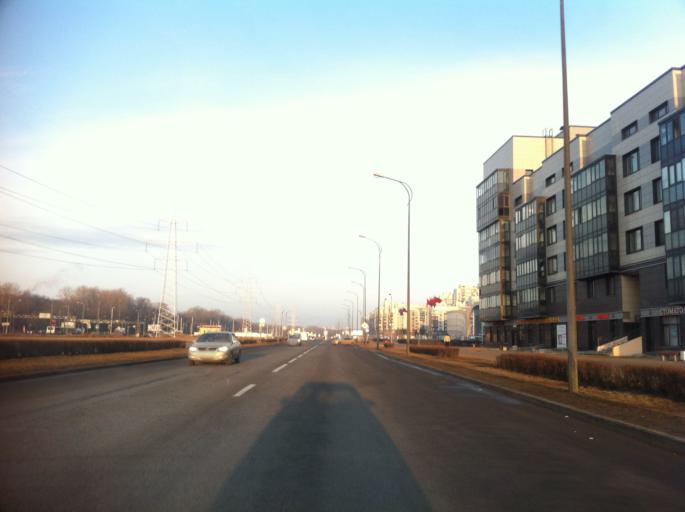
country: RU
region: St.-Petersburg
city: Sosnovaya Polyana
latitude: 59.8477
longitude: 30.1518
